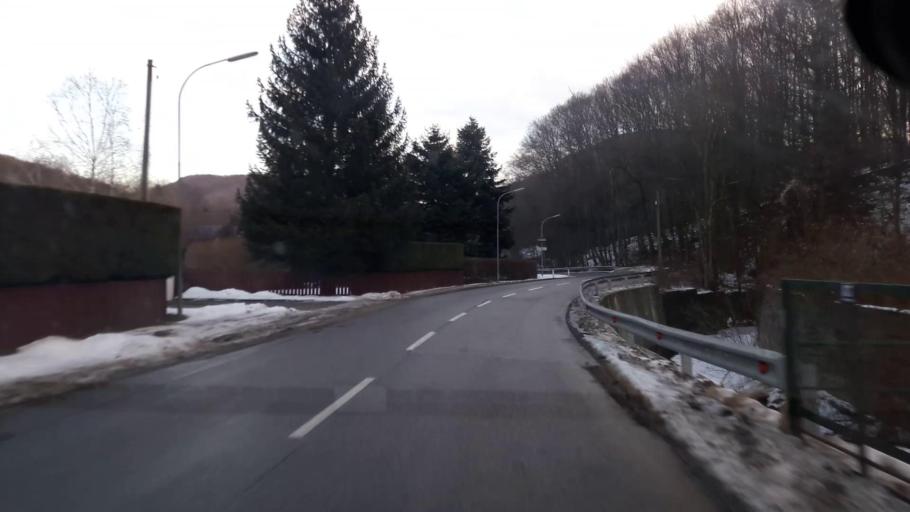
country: AT
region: Lower Austria
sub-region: Politischer Bezirk Wien-Umgebung
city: Klosterneuburg
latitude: 48.2668
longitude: 16.2575
